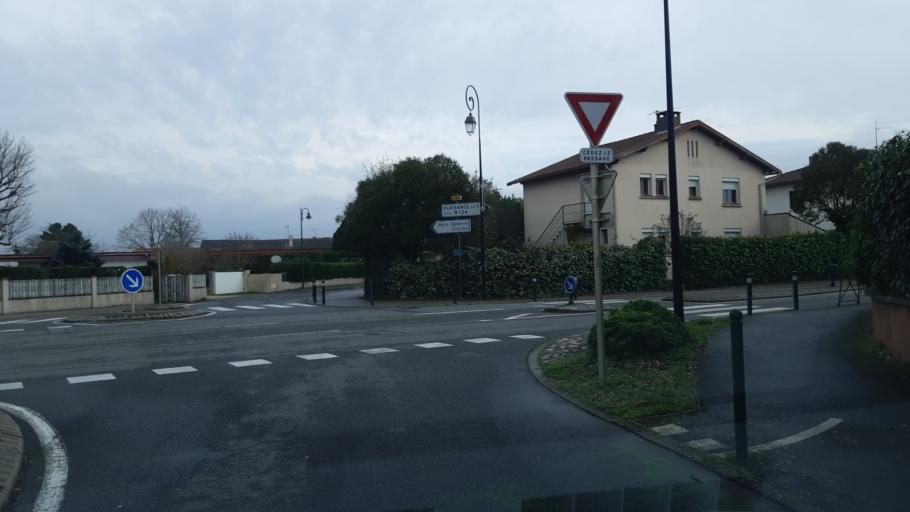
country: FR
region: Midi-Pyrenees
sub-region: Departement de la Haute-Garonne
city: Pibrac
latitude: 43.6130
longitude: 1.2855
